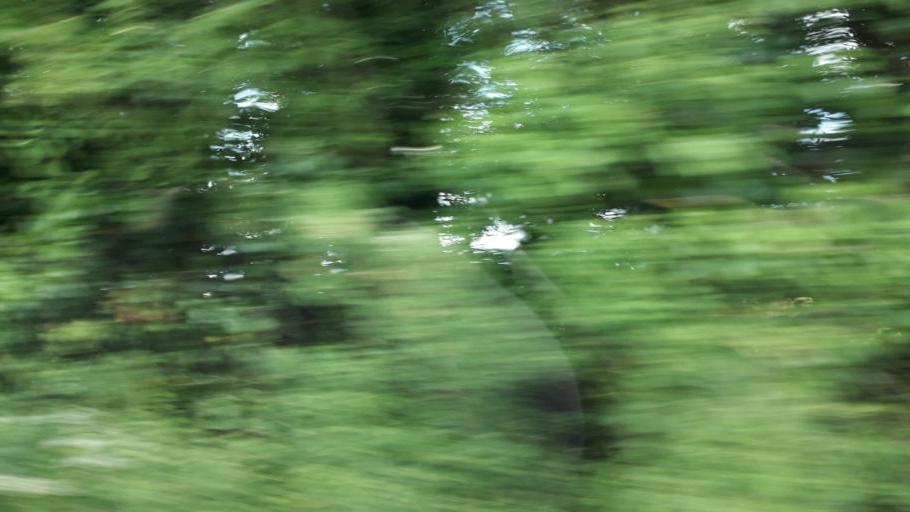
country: IE
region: Leinster
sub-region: Kildare
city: Moone
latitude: 53.0136
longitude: -6.8050
